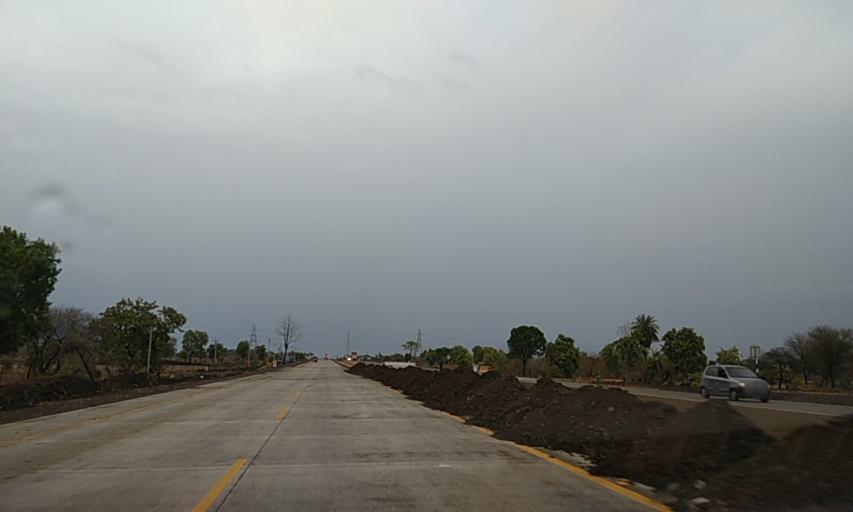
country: IN
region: Madhya Pradesh
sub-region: Rajgarh
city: Sarangpur
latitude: 23.6304
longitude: 76.5728
